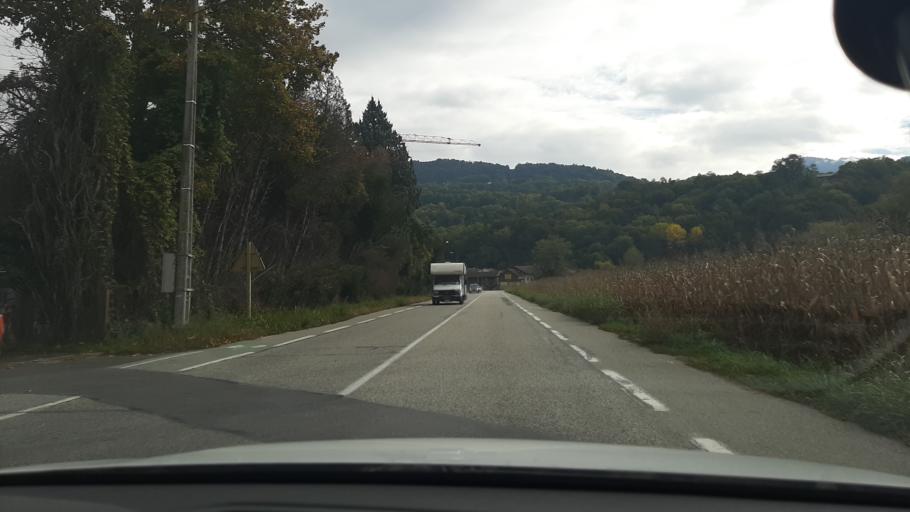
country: FR
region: Rhone-Alpes
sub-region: Departement de la Savoie
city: Montmelian
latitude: 45.4621
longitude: 6.0481
